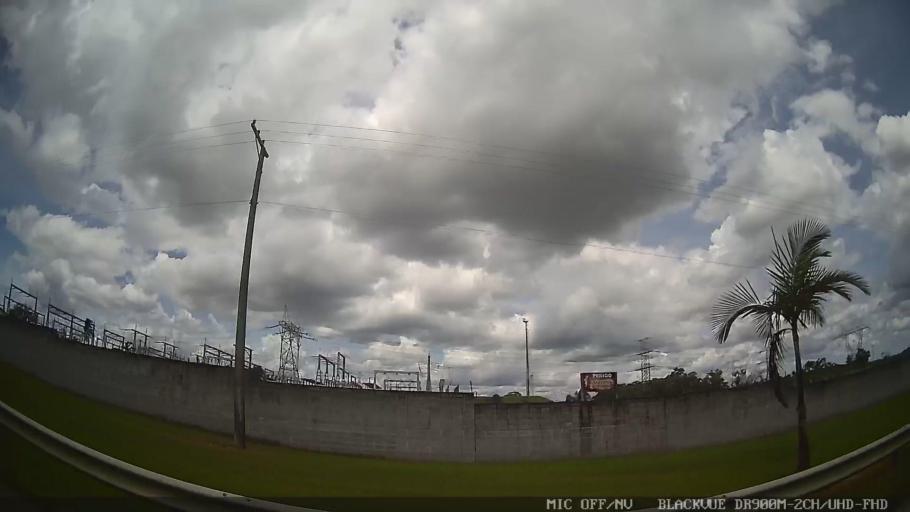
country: BR
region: Sao Paulo
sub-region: Suzano
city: Suzano
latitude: -23.5887
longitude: -46.2563
